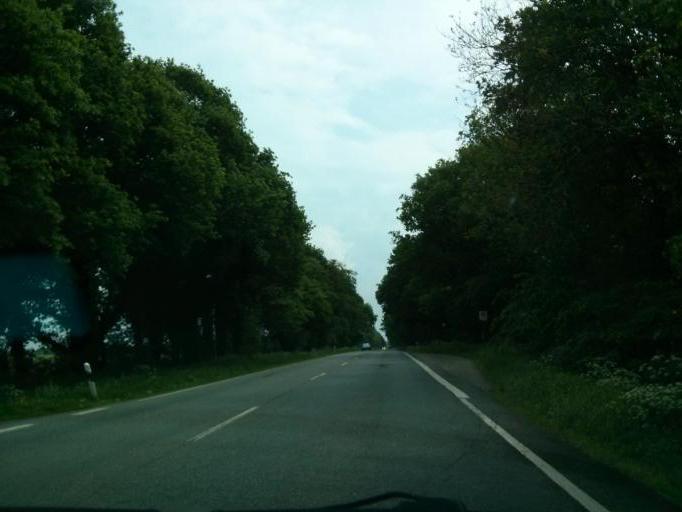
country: DE
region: Lower Saxony
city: Loxstedt
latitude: 53.4917
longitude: 8.6515
